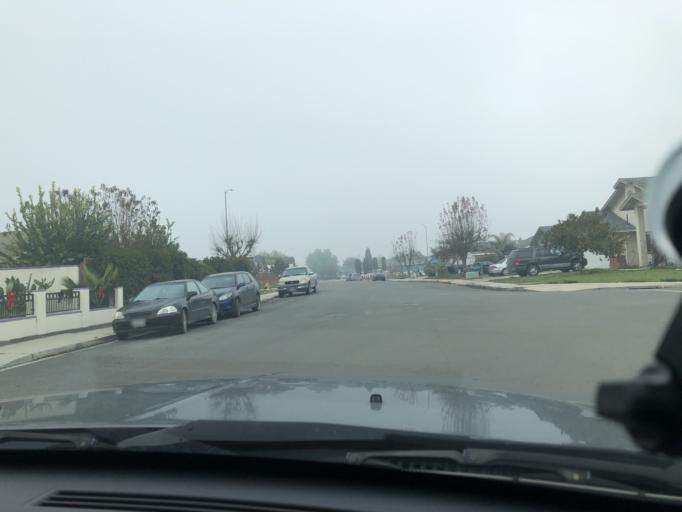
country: US
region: California
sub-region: Monterey County
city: King City
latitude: 36.2062
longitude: -121.1429
